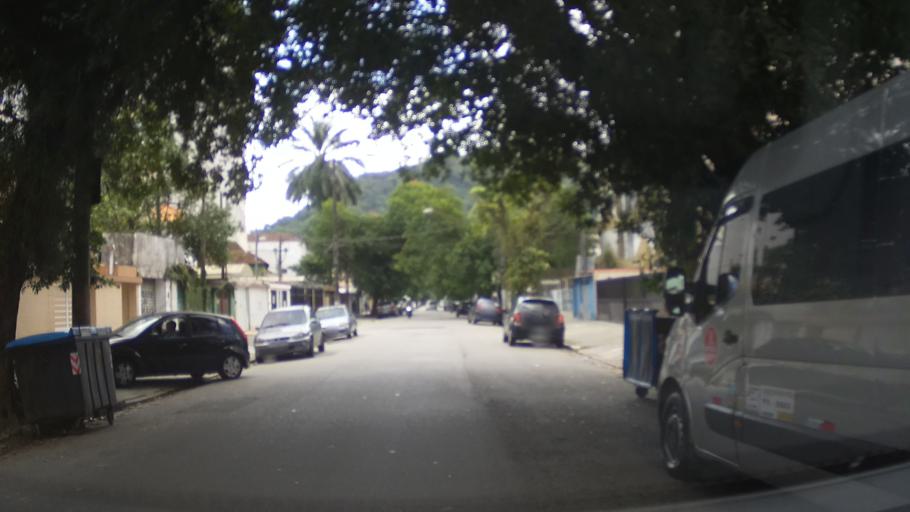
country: BR
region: Sao Paulo
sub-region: Santos
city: Santos
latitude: -23.9474
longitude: -46.3328
